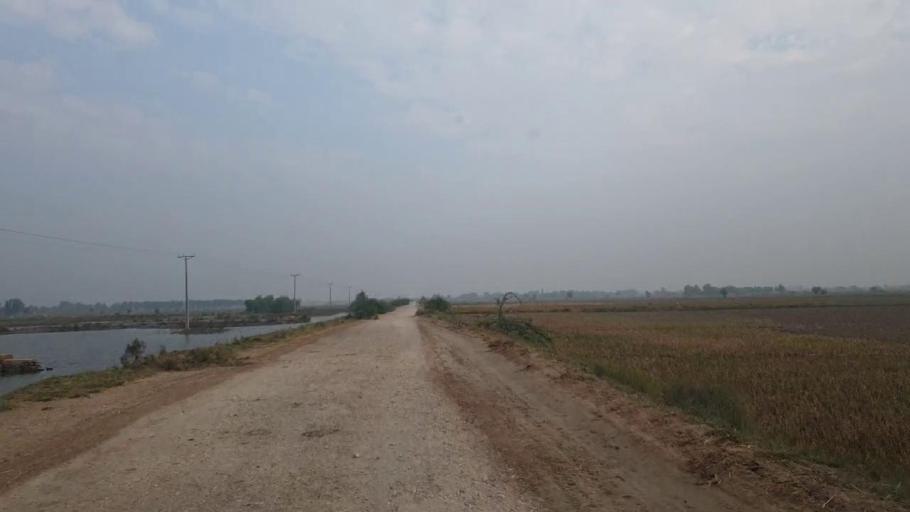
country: PK
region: Sindh
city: Talhar
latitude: 24.8163
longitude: 68.8767
